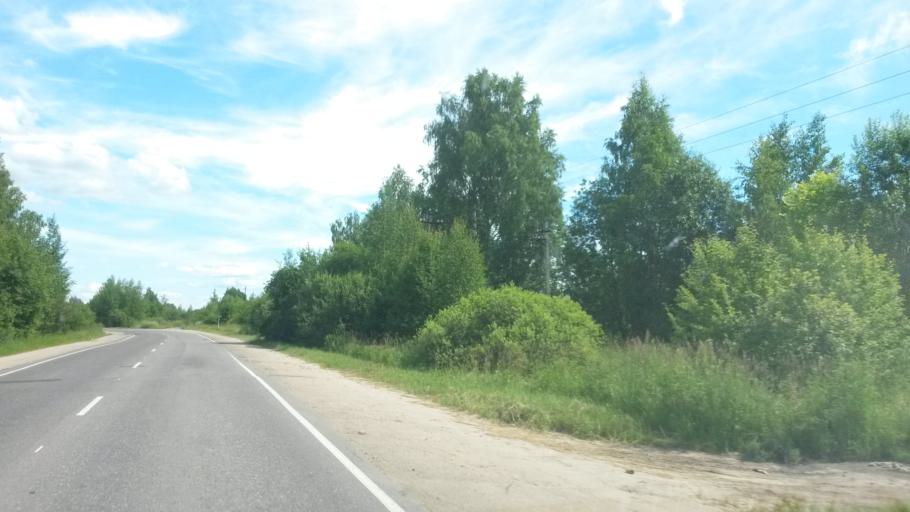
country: RU
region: Ivanovo
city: Zavolzhsk
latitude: 57.5038
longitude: 42.1064
